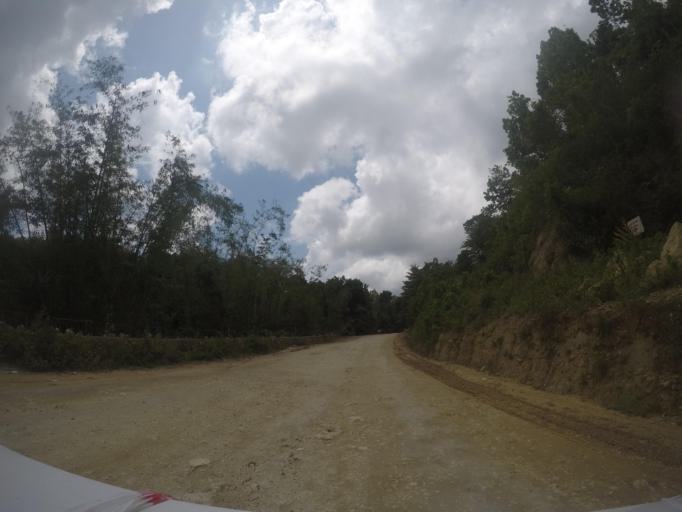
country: TL
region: Baucau
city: Venilale
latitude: -8.5752
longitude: 126.3896
